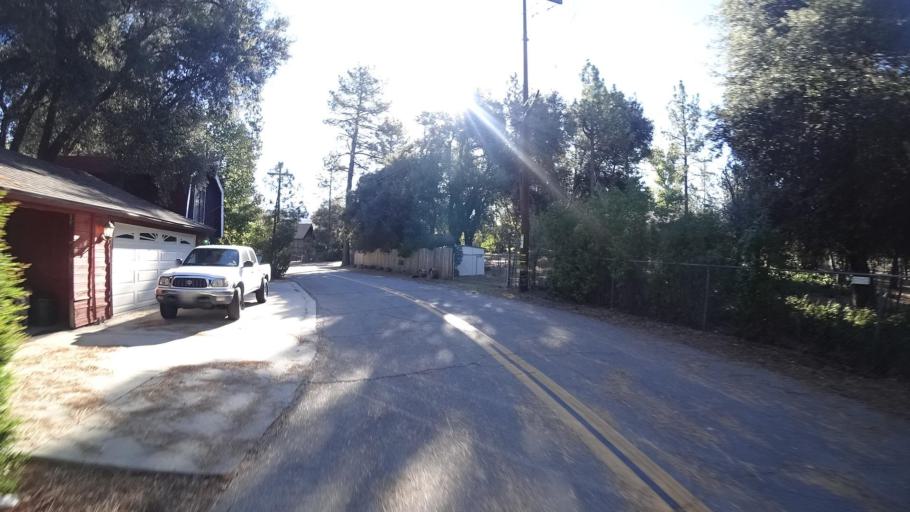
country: US
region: California
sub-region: San Diego County
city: Pine Valley
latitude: 32.8276
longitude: -116.5274
